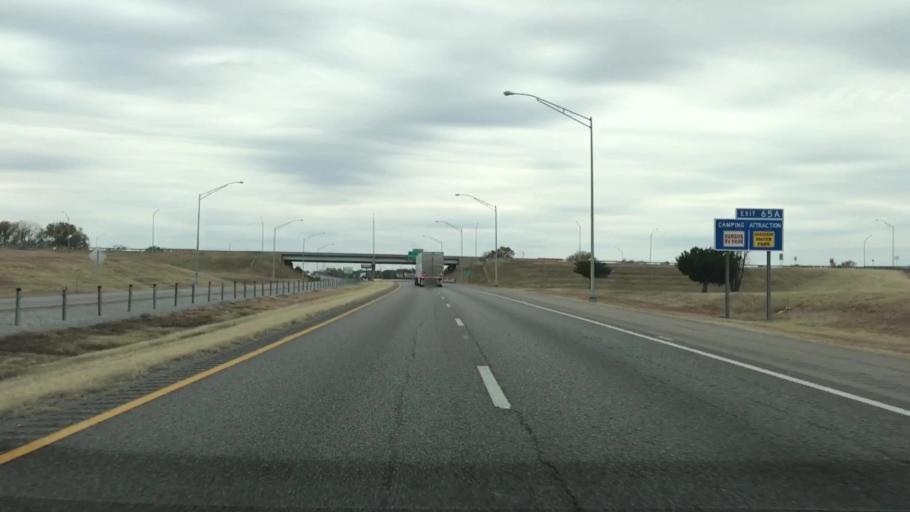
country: US
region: Oklahoma
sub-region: Custer County
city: Clinton
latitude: 35.5006
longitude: -98.9619
